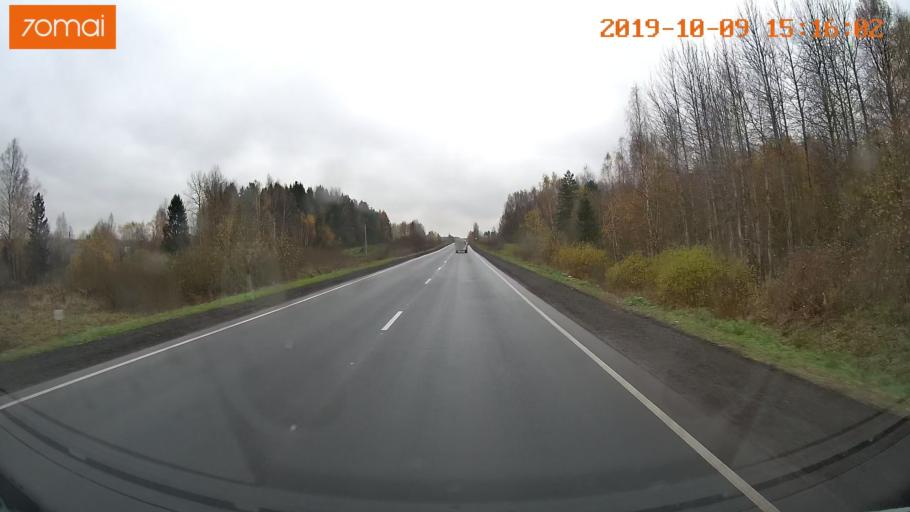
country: RU
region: Kostroma
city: Susanino
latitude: 58.1149
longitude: 41.5873
